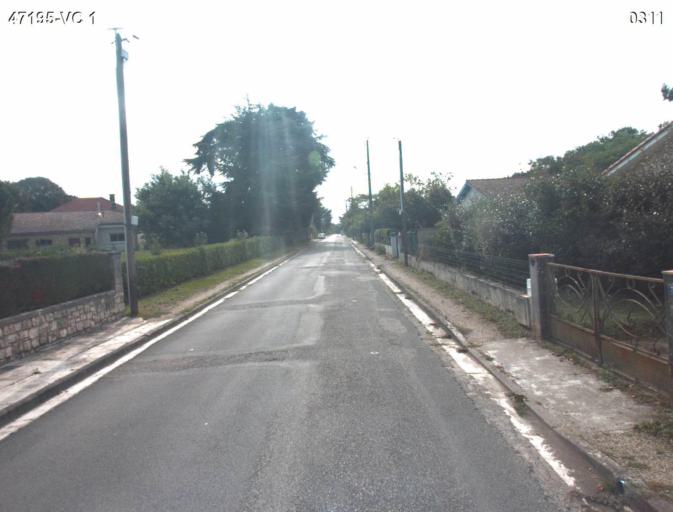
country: FR
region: Aquitaine
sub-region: Departement du Lot-et-Garonne
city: Nerac
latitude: 44.1303
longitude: 0.3443
